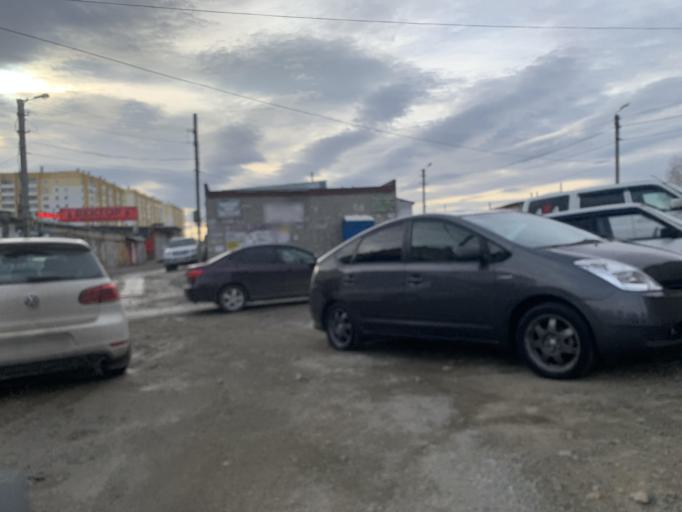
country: RU
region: Chelyabinsk
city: Roshchino
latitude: 55.1931
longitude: 61.2768
